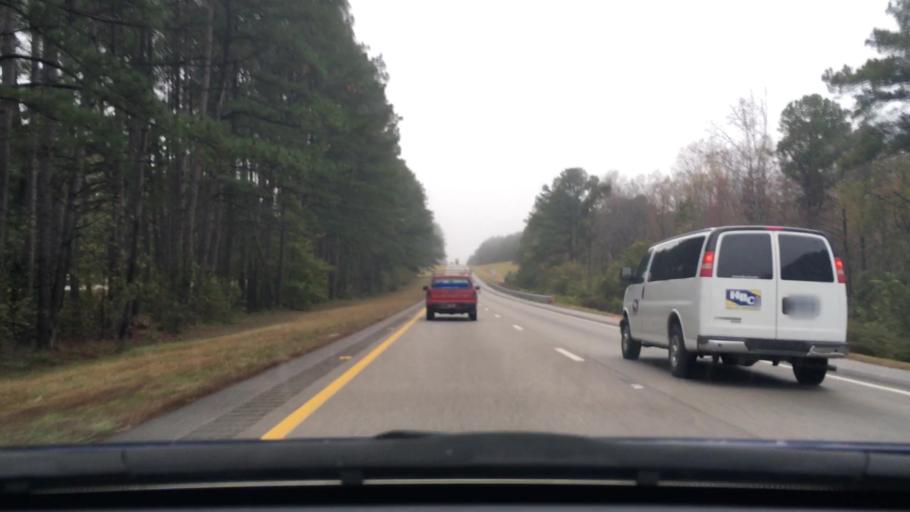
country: US
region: South Carolina
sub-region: Kershaw County
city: Camden
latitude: 34.2085
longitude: -80.4570
